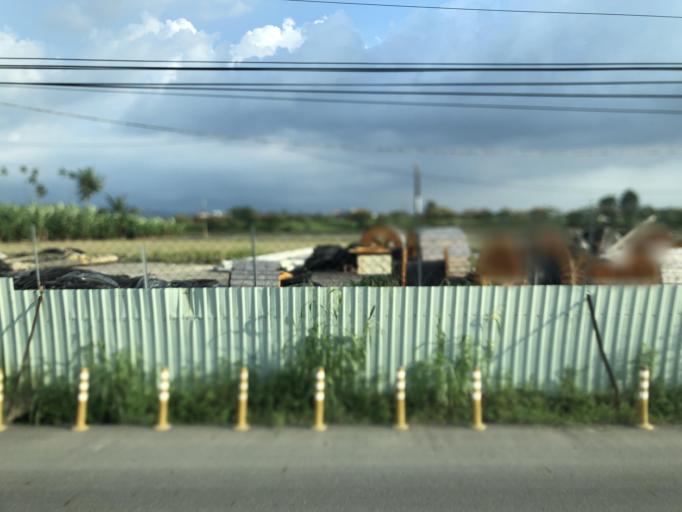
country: TW
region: Taiwan
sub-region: Pingtung
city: Pingtung
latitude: 22.9005
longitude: 120.5270
